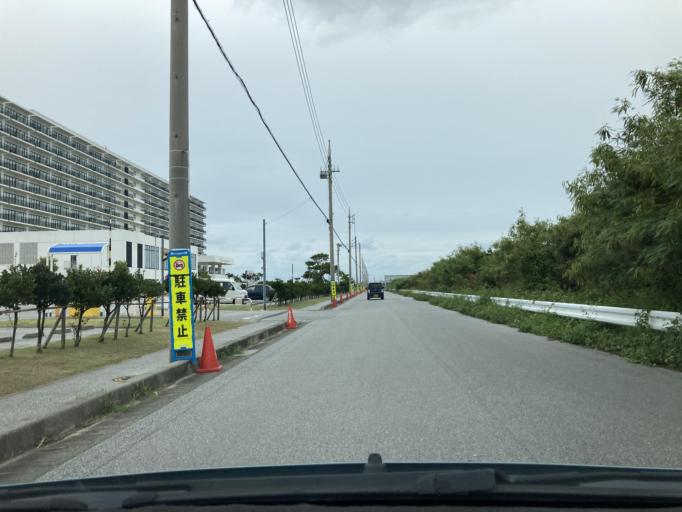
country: JP
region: Okinawa
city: Itoman
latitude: 26.1308
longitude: 127.6541
